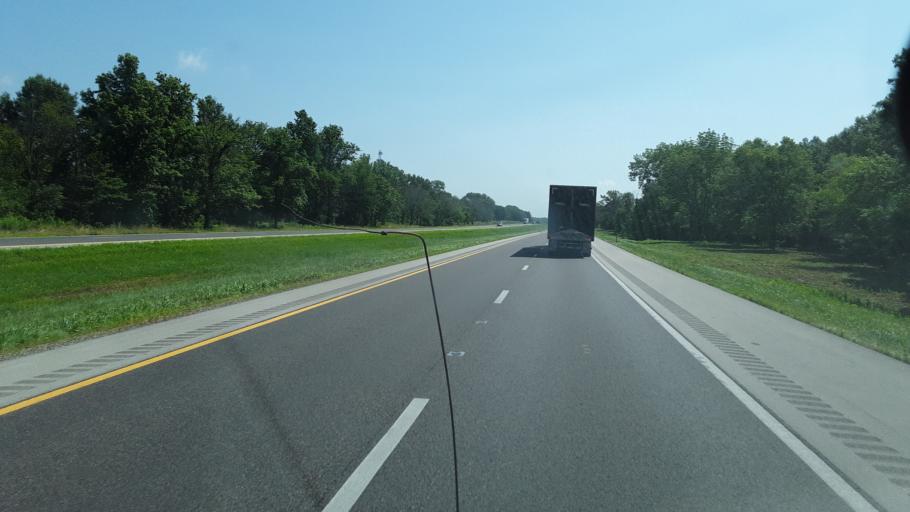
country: US
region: Illinois
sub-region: Cumberland County
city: Toledo
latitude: 39.1967
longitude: -88.3102
